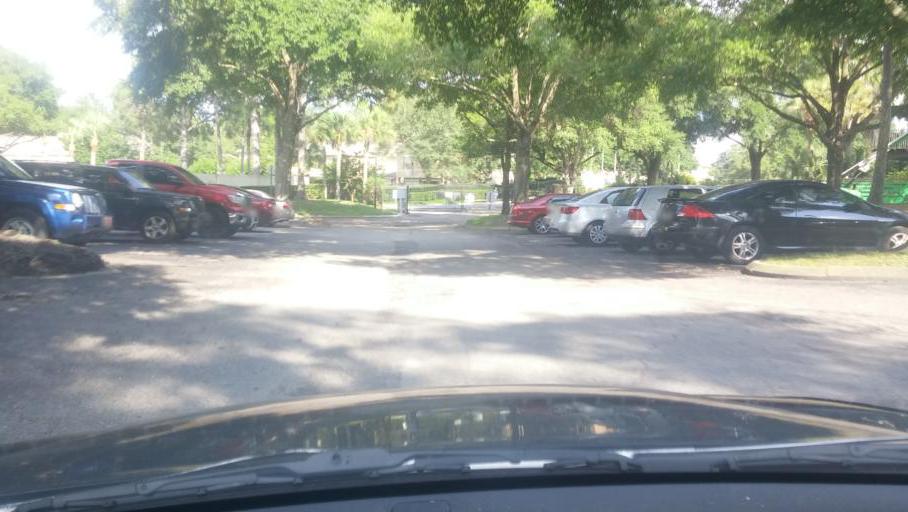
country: US
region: Florida
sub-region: Seminole County
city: Forest City
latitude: 28.6591
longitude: -81.4246
